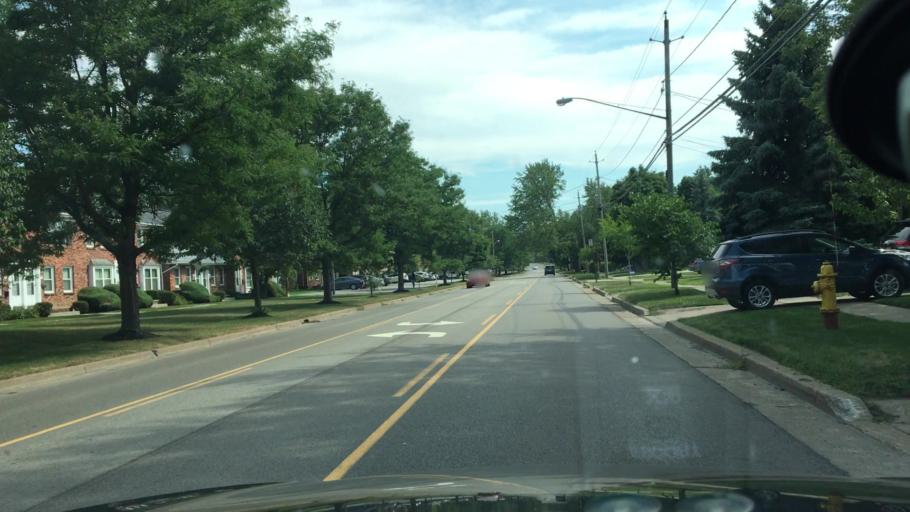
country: US
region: New York
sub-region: Erie County
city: Williamsville
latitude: 42.9732
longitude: -78.7395
